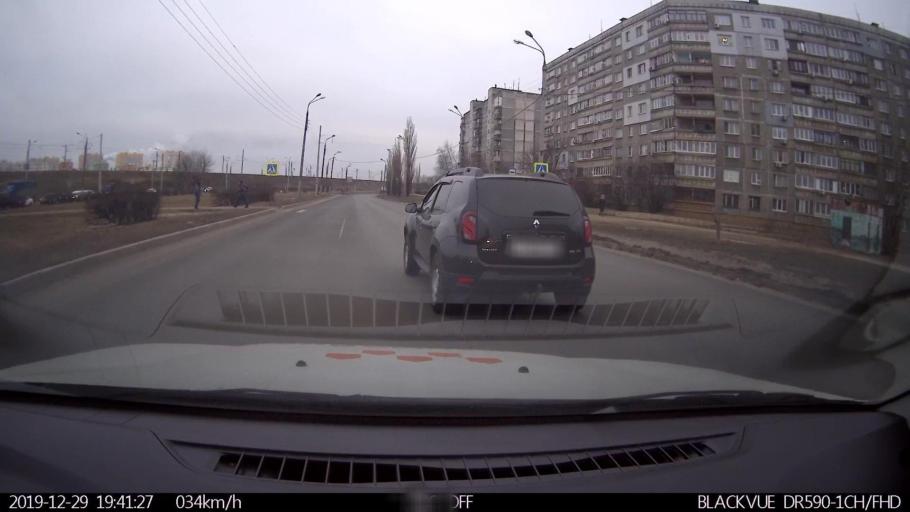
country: RU
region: Nizjnij Novgorod
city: Nizhniy Novgorod
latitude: 56.3397
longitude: 43.9237
